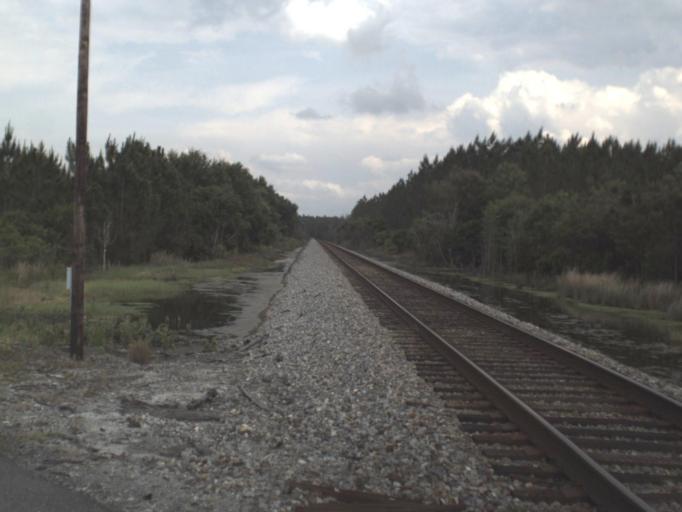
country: US
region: Florida
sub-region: Baker County
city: Macclenny
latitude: 30.5119
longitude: -82.2535
